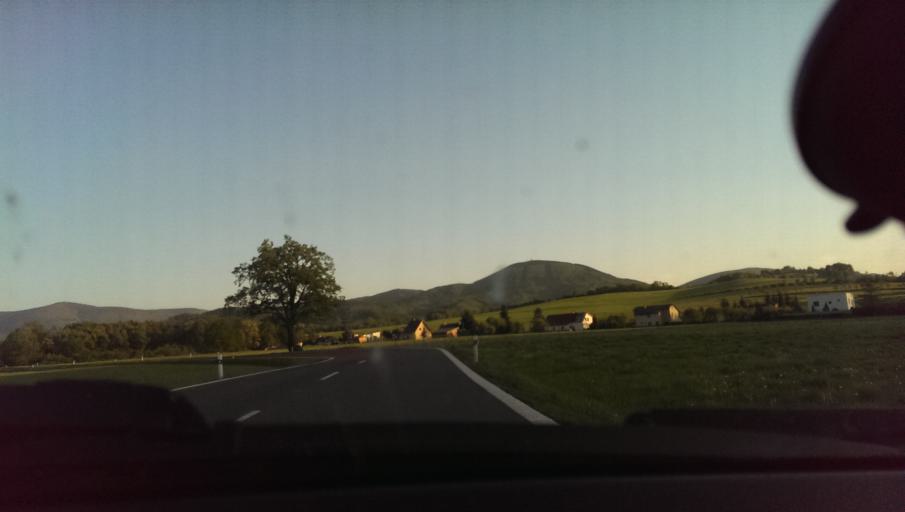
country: CZ
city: Lichnov (o. Novy Jicin)
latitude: 49.5698
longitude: 18.1857
